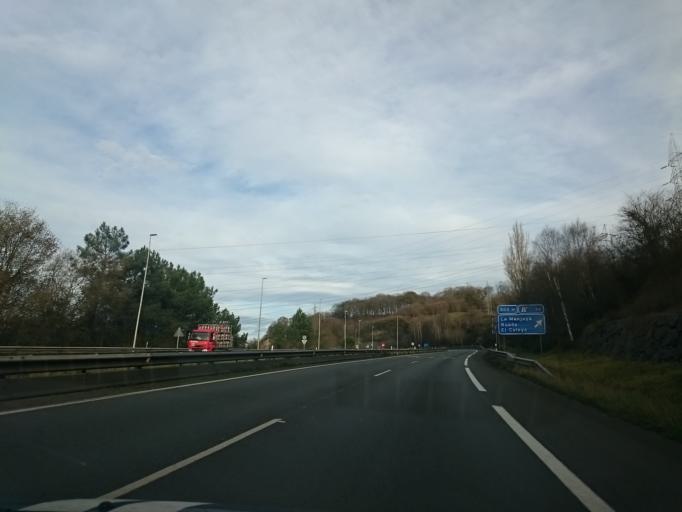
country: ES
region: Asturias
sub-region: Province of Asturias
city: Oviedo
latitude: 43.3211
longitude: -5.8702
